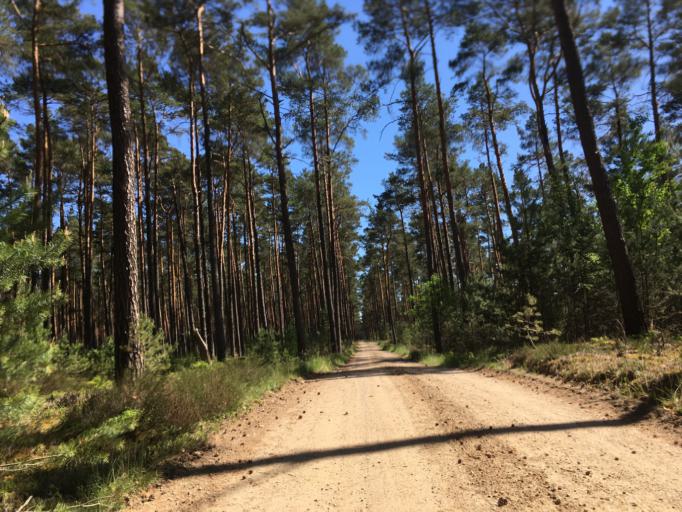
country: DE
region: Brandenburg
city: Friedrichswalde
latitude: 52.9685
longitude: 13.6361
